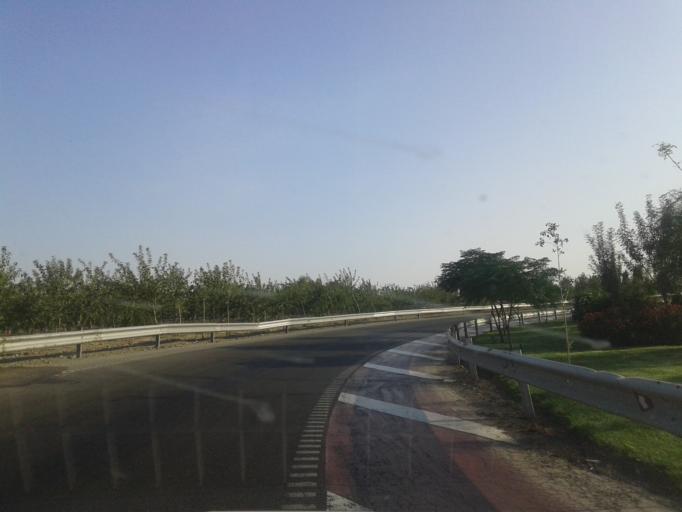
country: IR
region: Tehran
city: Eslamshahr
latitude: 35.6491
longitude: 51.2747
